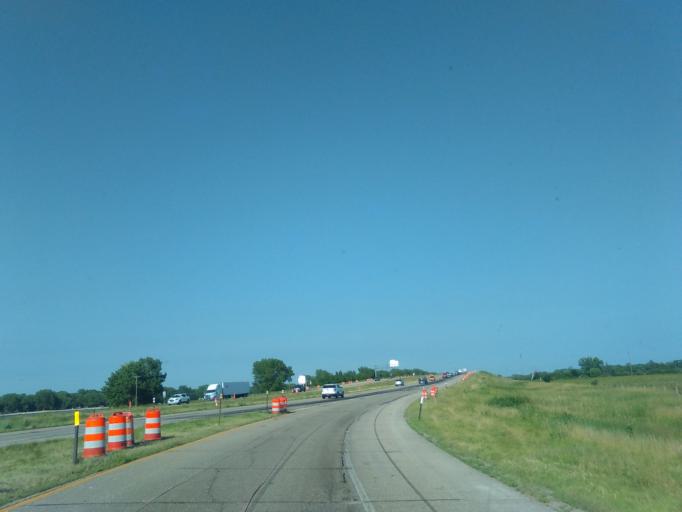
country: US
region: Nebraska
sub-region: Hall County
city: Grand Island
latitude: 40.8204
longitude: -98.3752
